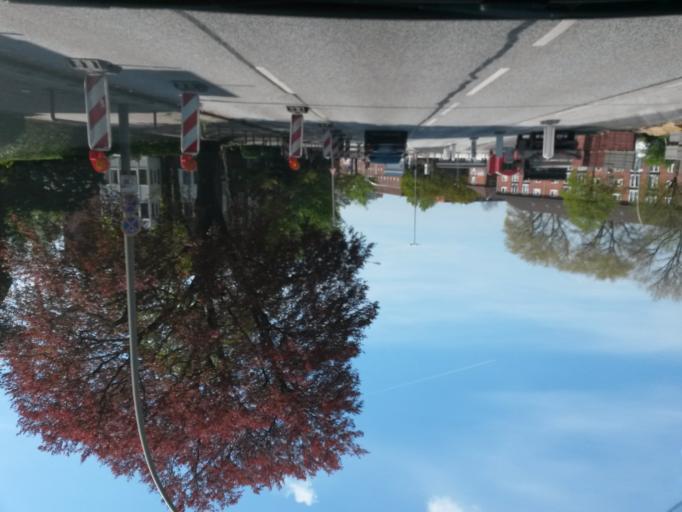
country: DE
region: Hamburg
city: Altona
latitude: 53.5657
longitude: 9.9091
